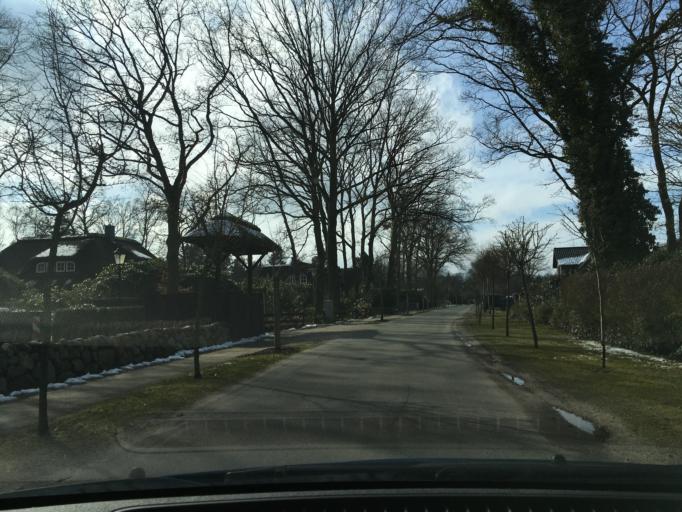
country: DE
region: Lower Saxony
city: Barum
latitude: 53.3335
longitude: 10.4062
